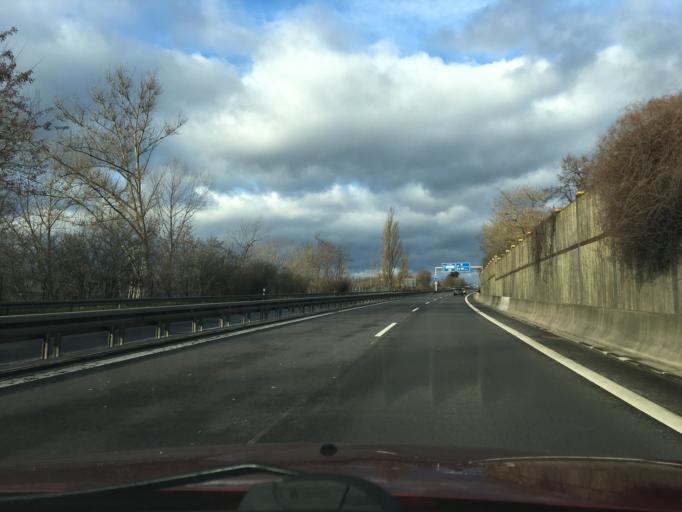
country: DE
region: Berlin
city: Bohnsdorf
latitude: 52.3963
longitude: 13.5611
